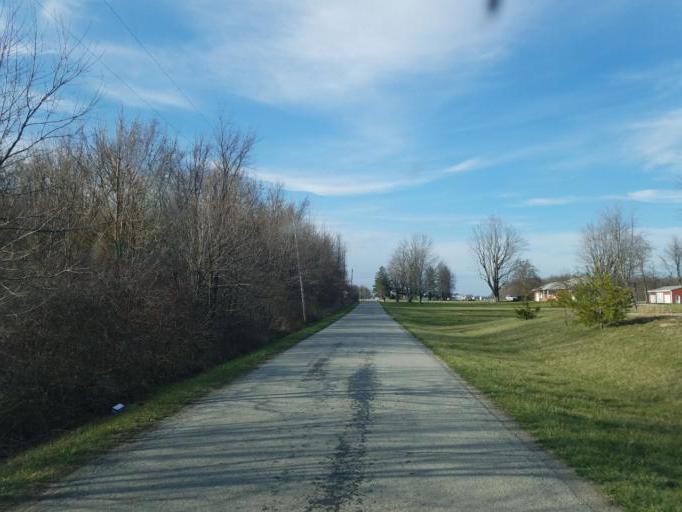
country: US
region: Ohio
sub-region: Crawford County
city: Galion
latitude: 40.7700
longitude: -82.8727
